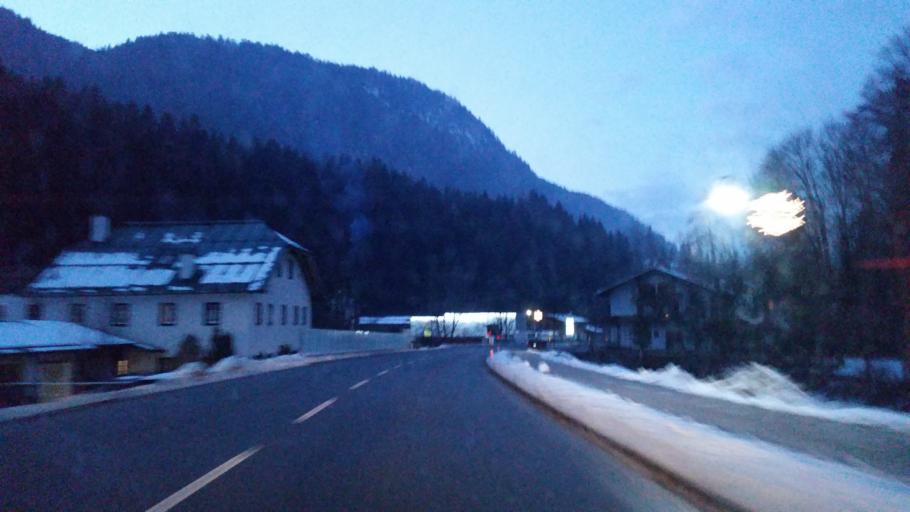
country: AT
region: Salzburg
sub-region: Politischer Bezirk Hallein
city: Abtenau
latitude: 47.5098
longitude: 13.4322
